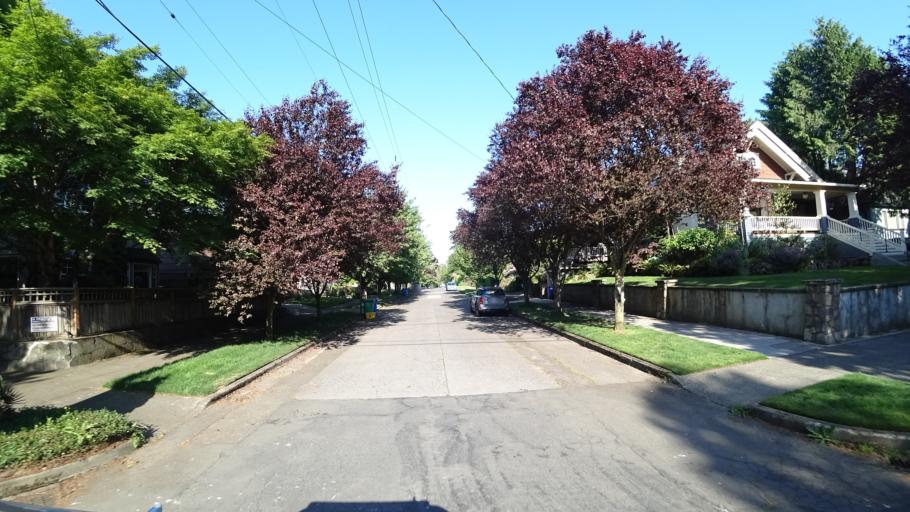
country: US
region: Oregon
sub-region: Multnomah County
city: Portland
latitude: 45.5436
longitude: -122.6359
